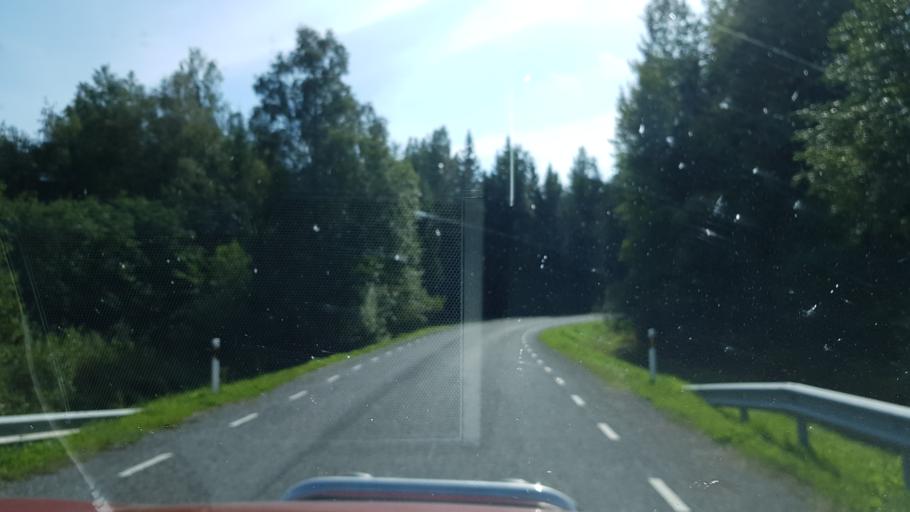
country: EE
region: Viljandimaa
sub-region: Viljandi linn
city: Viljandi
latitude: 58.3215
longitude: 25.5270
